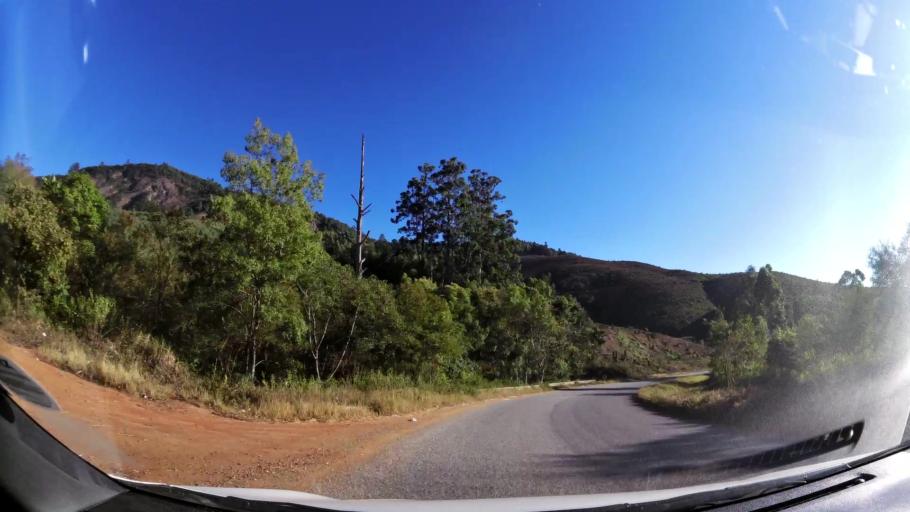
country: ZA
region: Limpopo
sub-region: Mopani District Municipality
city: Tzaneen
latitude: -23.9481
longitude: 30.0133
